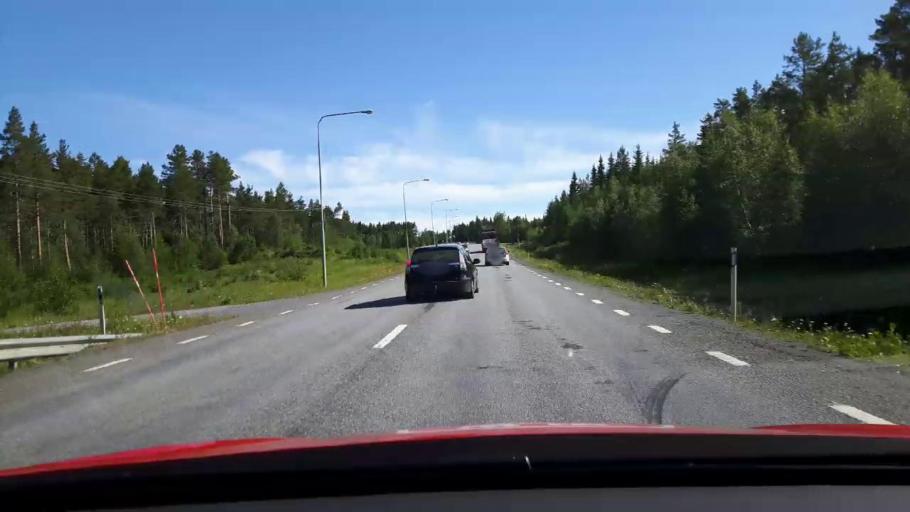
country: SE
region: Jaemtland
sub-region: OEstersunds Kommun
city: Lit
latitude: 63.3774
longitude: 14.8842
